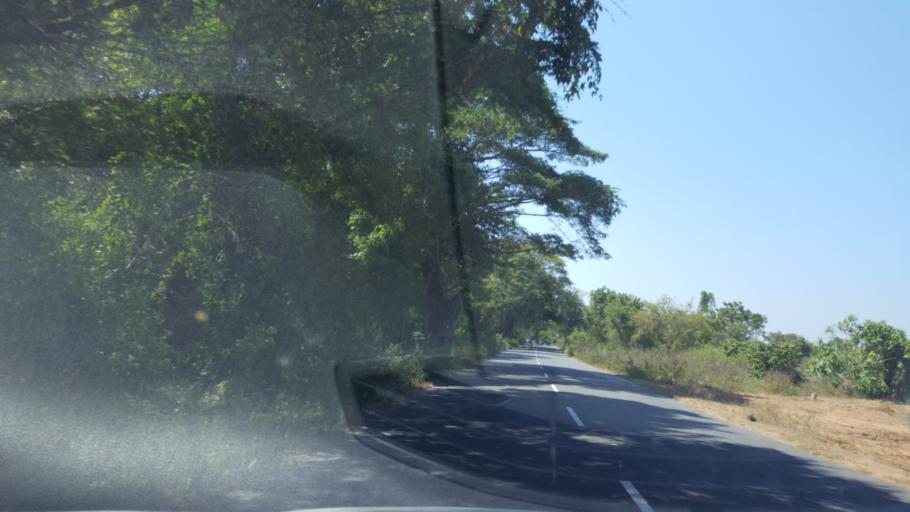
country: IN
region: Tamil Nadu
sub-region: Kancheepuram
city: Chengalpattu
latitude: 12.7527
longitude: 79.9311
